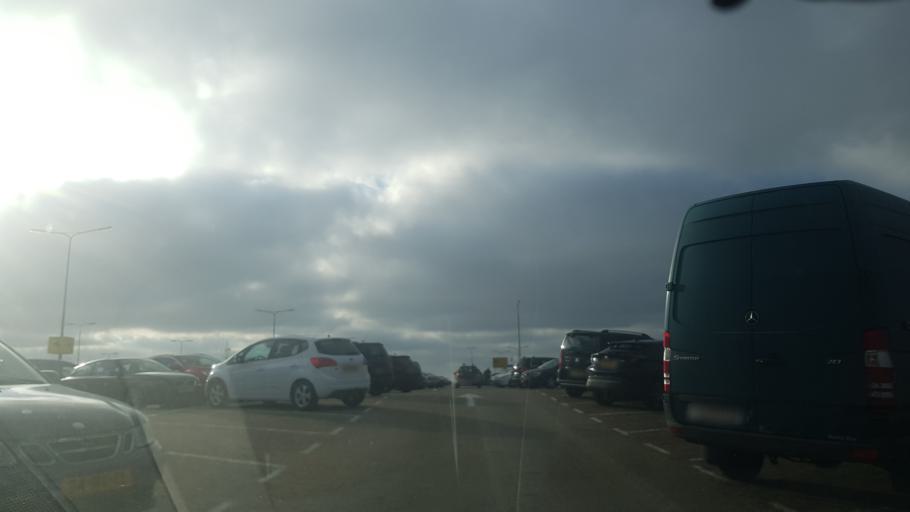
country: NL
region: Friesland
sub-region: Gemeente Dongeradeel
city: Holwerd
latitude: 53.3934
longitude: 5.8829
